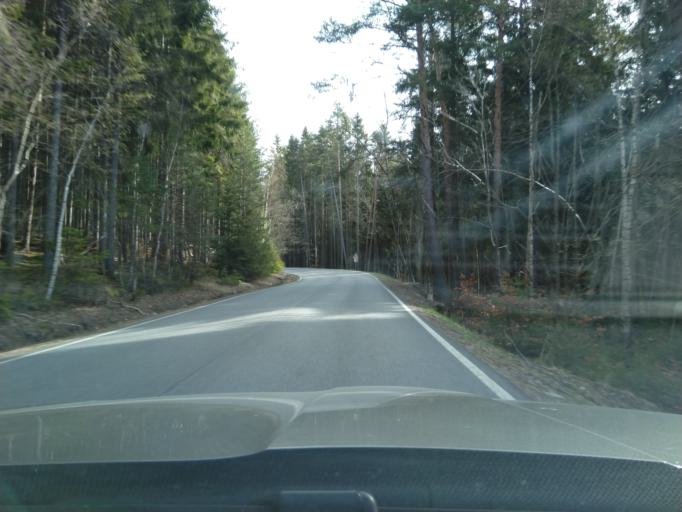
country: CZ
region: Jihocesky
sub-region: Okres Prachatice
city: Stachy
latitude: 49.0795
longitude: 13.6373
